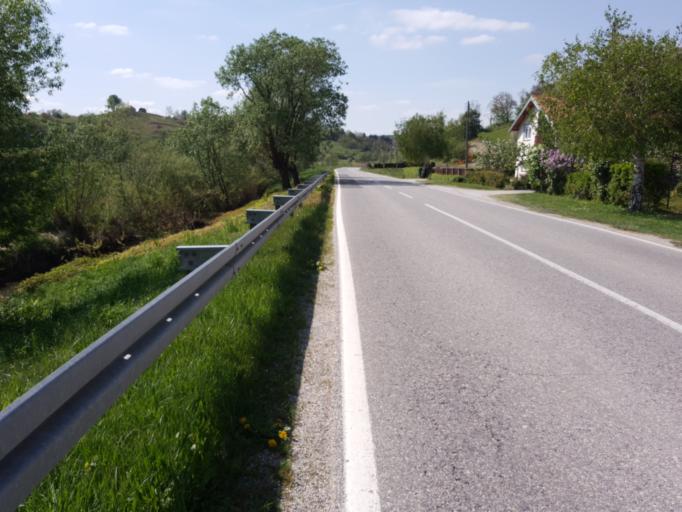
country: HR
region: Varazdinska
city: Lepoglava
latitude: 46.2260
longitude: 15.9701
